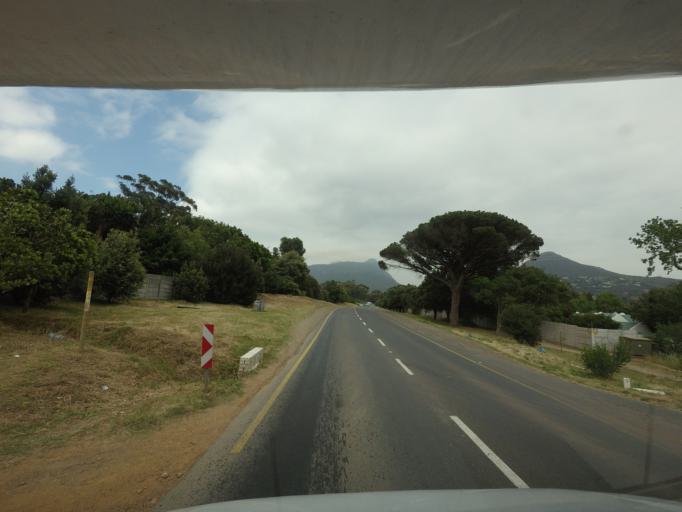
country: ZA
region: Western Cape
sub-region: City of Cape Town
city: Constantia
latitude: -34.0209
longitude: 18.3703
